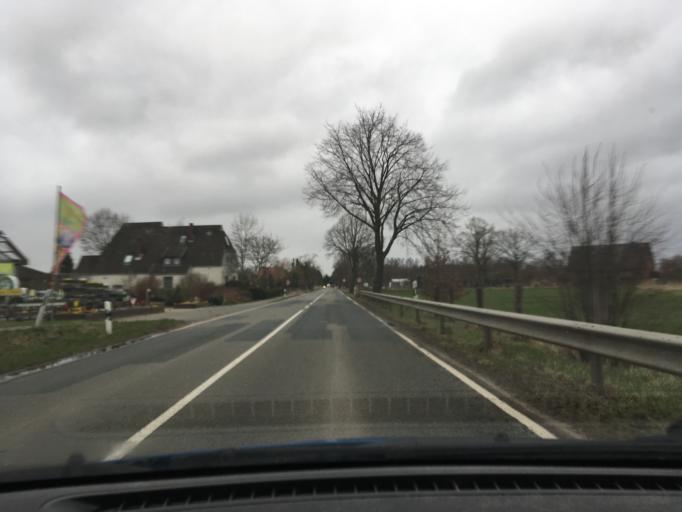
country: DE
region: Lower Saxony
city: Winsen
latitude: 53.3781
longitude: 10.2458
